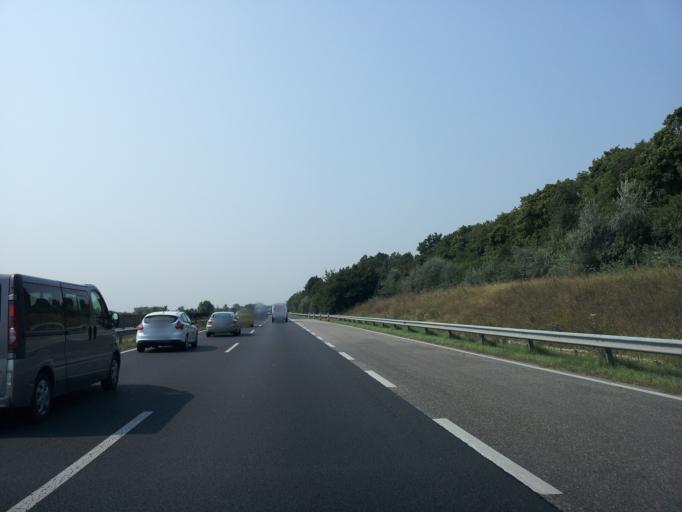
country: HU
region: Pest
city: Tarnok
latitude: 47.3795
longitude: 18.8336
